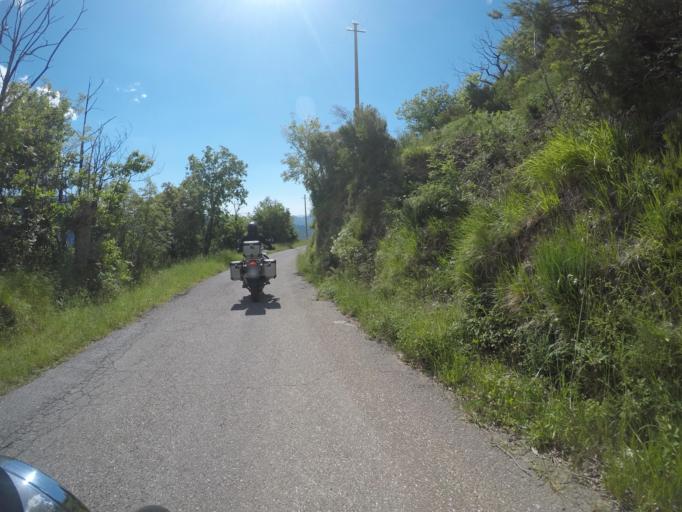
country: IT
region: Tuscany
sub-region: Provincia di Massa-Carrara
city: Casola in Lunigiana
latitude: 44.1780
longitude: 10.1712
